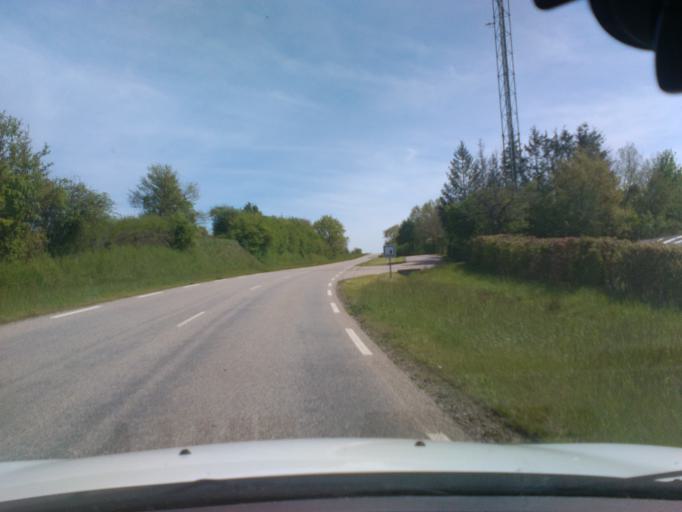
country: FR
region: Lorraine
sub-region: Departement des Vosges
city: Mirecourt
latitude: 48.3295
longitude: 6.1336
